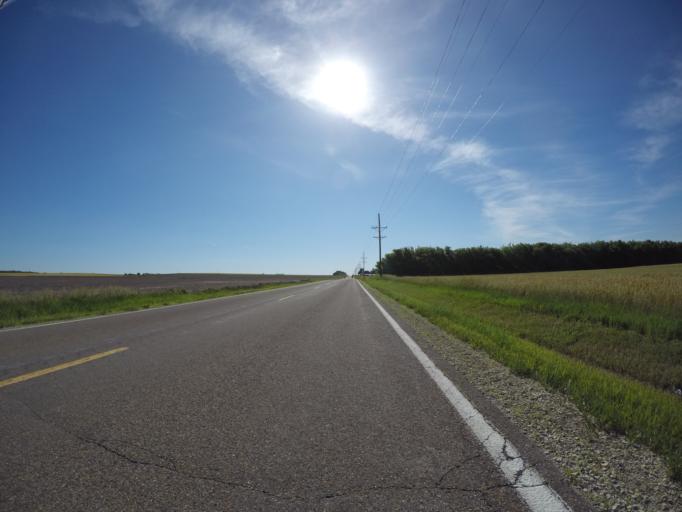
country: US
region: Kansas
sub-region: Mitchell County
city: Beloit
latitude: 39.6393
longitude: -97.9371
